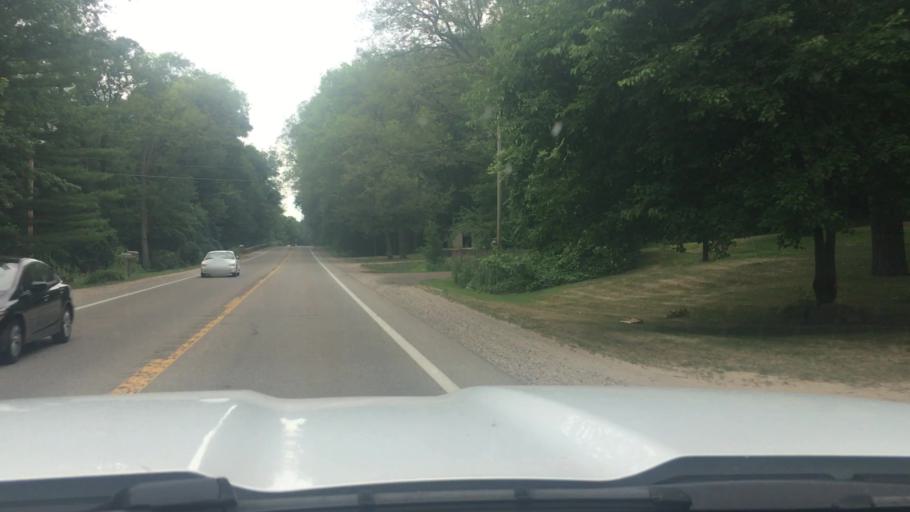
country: US
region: Michigan
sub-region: Ionia County
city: Saranac
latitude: 42.9354
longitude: -85.2266
